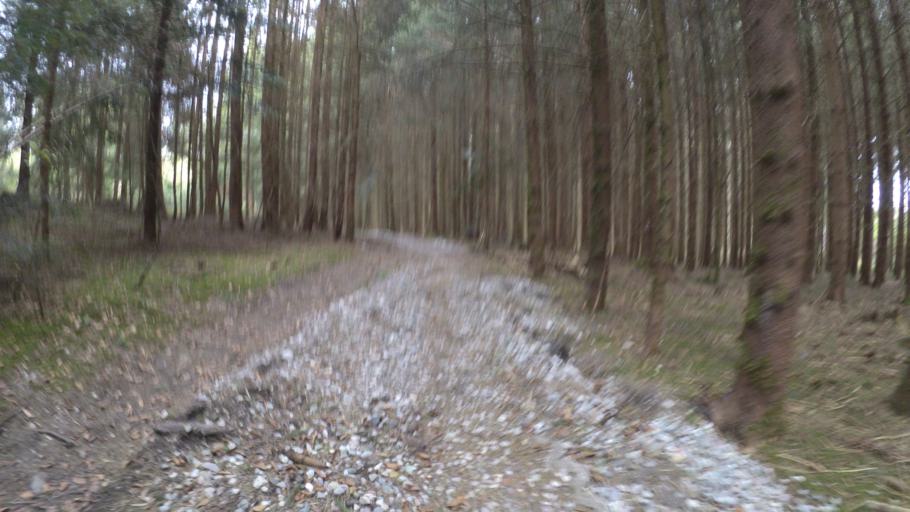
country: DE
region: Bavaria
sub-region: Upper Bavaria
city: Nussdorf
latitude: 47.9168
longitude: 12.5832
